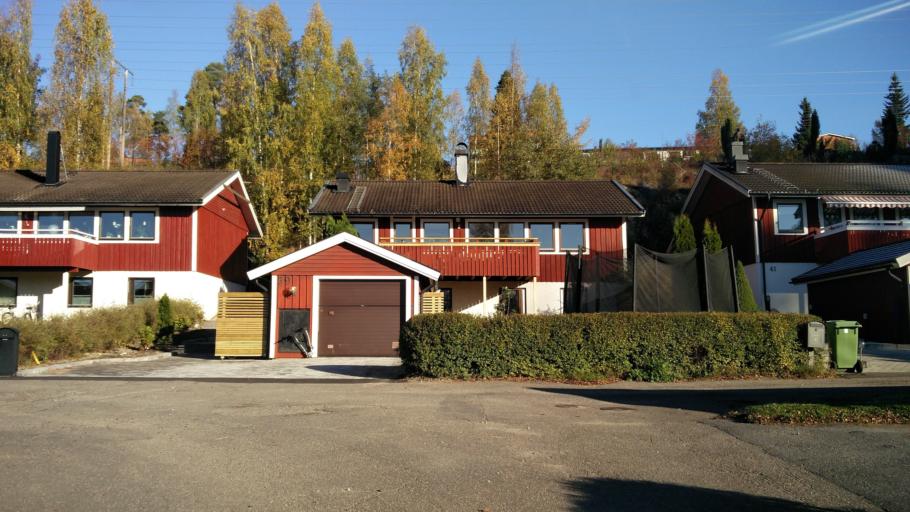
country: SE
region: Vaesternorrland
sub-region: Sundsvalls Kommun
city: Sundsvall
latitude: 62.4070
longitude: 17.2644
